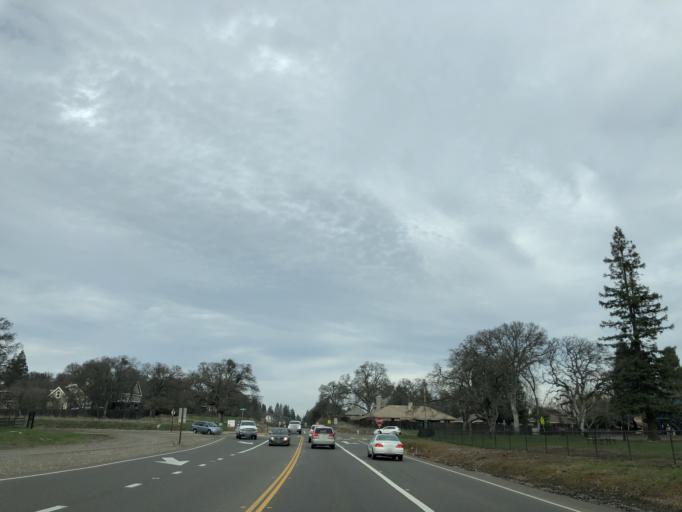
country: US
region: California
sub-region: El Dorado County
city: El Dorado Hills
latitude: 38.7016
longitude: -121.0828
